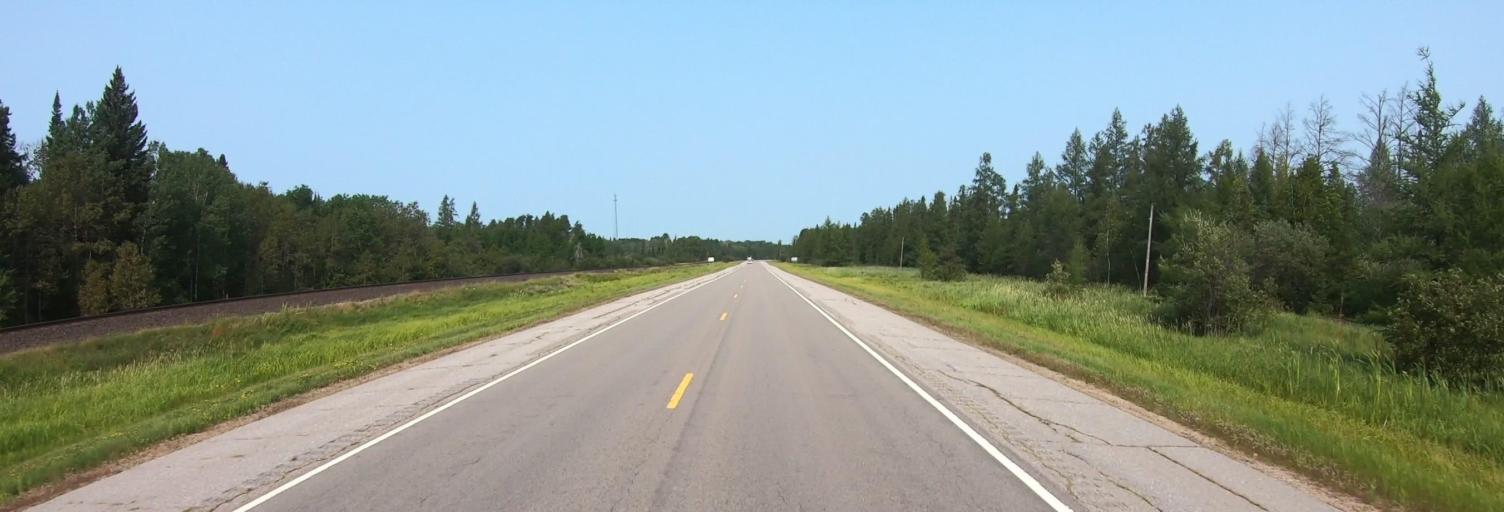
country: US
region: Minnesota
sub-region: Saint Louis County
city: Chisholm
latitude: 48.1435
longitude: -92.8604
